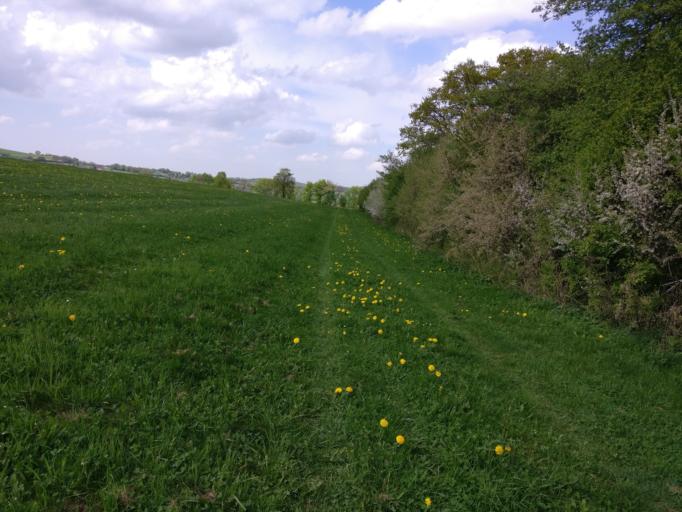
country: DE
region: Hesse
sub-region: Regierungsbezirk Giessen
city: Schwalmtal
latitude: 50.6507
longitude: 9.2751
